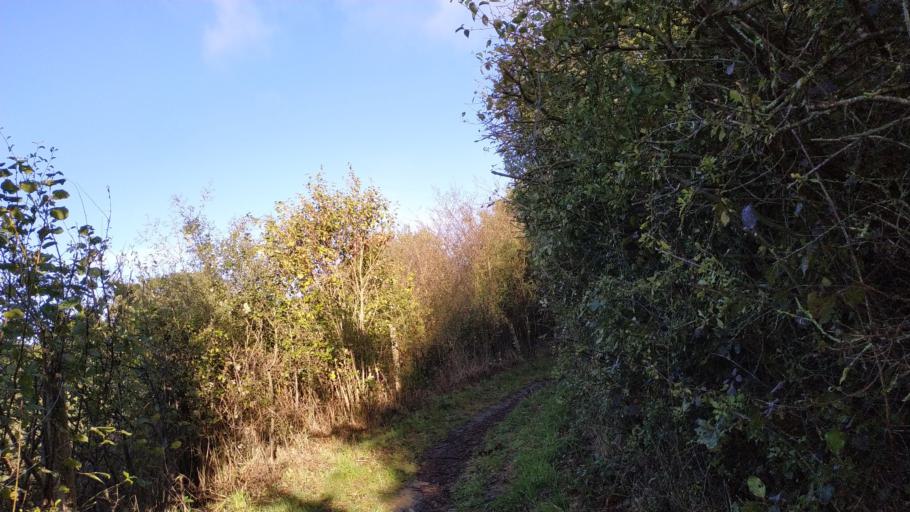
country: FR
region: Brittany
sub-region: Departement d'Ille-et-Vilaine
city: Chantepie
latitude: 48.0785
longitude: -1.6226
